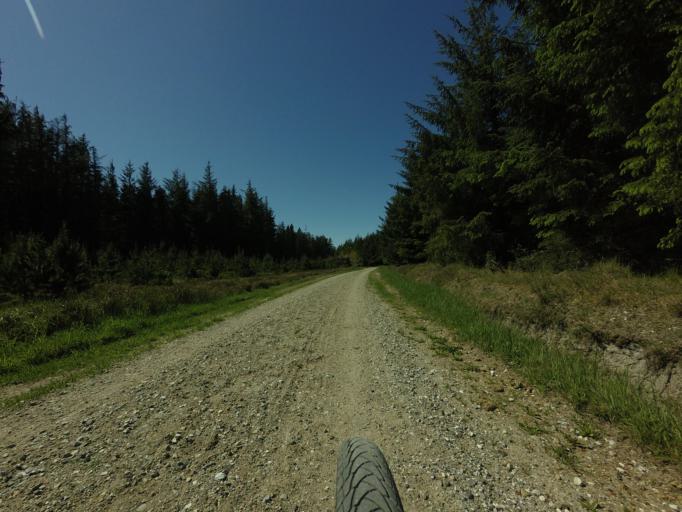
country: DK
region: North Denmark
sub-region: Jammerbugt Kommune
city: Pandrup
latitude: 57.2296
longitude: 9.5731
